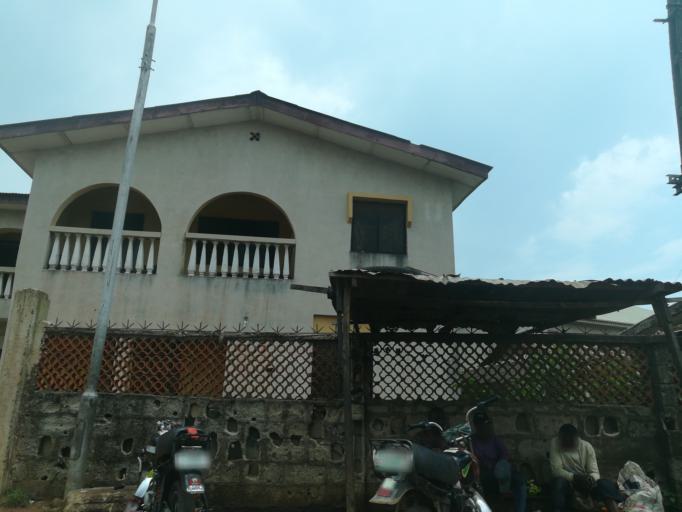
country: NG
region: Lagos
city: Ikorodu
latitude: 6.5654
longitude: 3.5914
